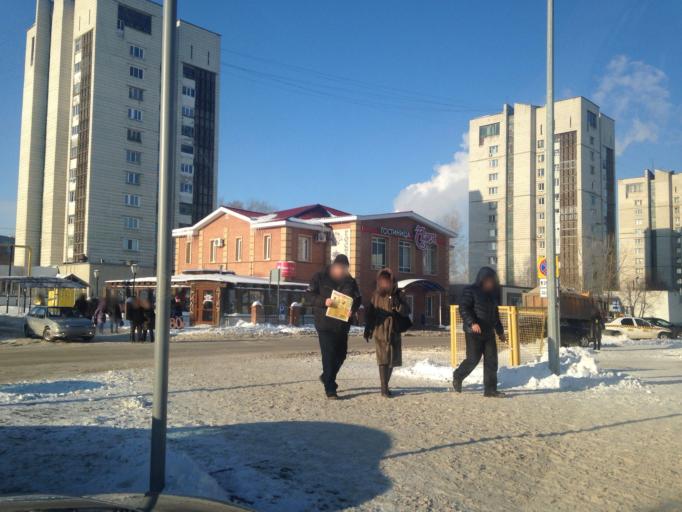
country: RU
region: Ulyanovsk
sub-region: Ulyanovskiy Rayon
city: Ulyanovsk
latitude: 54.3061
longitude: 48.3573
